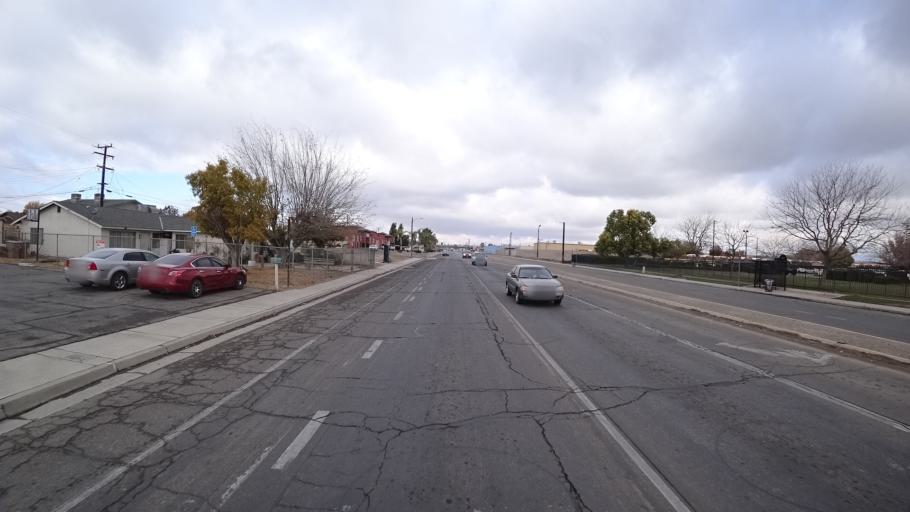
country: US
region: California
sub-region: Kern County
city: Bakersfield
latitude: 35.3469
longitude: -118.9855
